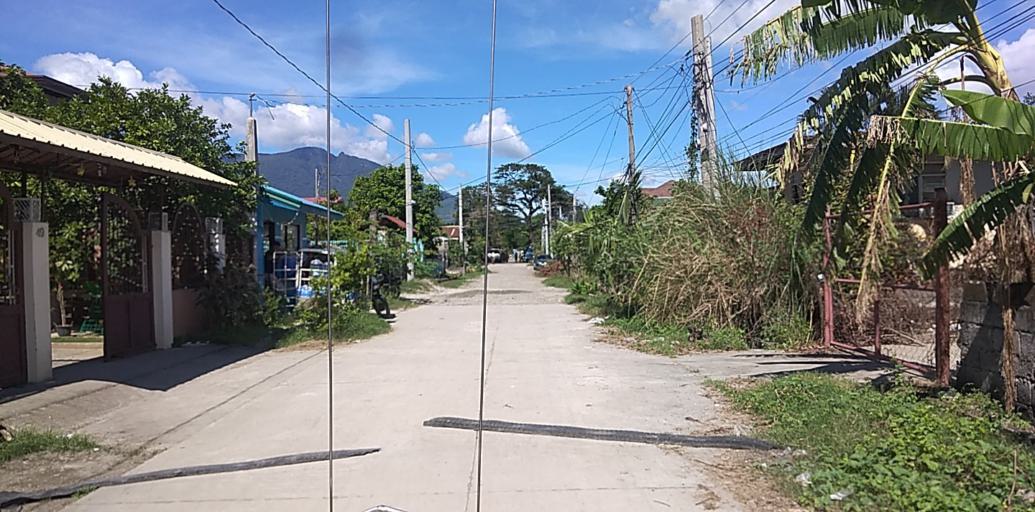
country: PH
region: Central Luzon
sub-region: Province of Pampanga
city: Arayat
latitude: 15.1371
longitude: 120.7747
